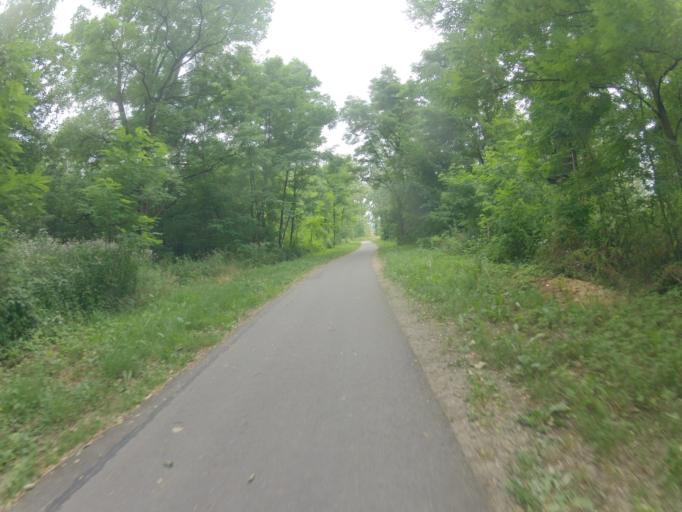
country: PL
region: Lesser Poland Voivodeship
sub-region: Powiat nowosadecki
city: Stary Sacz
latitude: 49.5380
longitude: 20.6581
